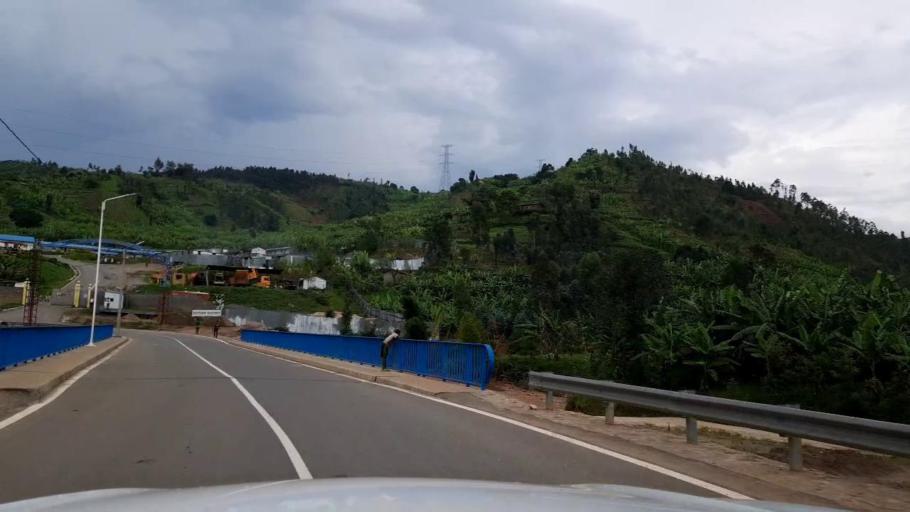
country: RW
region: Western Province
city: Kibuye
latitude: -2.0309
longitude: 29.3993
